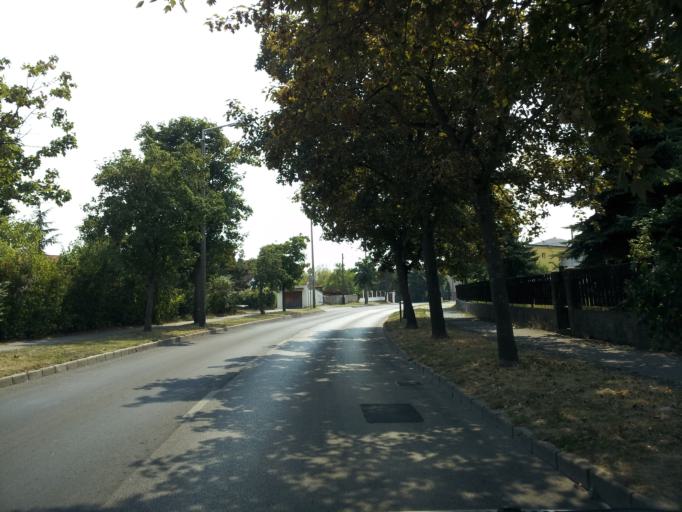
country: HU
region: Veszprem
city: Veszprem
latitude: 47.1010
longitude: 17.9251
